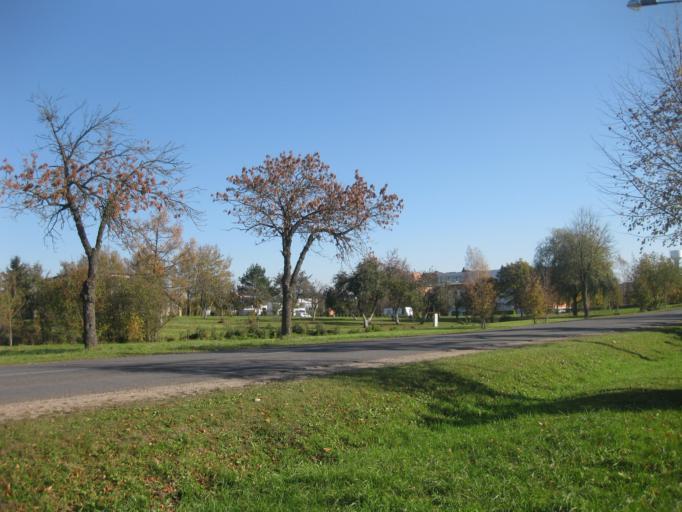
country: LT
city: Vilkija
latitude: 55.0471
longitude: 23.5739
